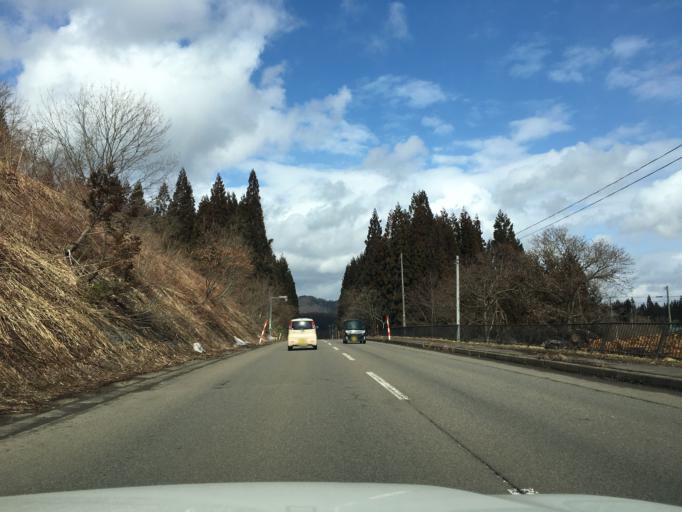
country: JP
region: Akita
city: Takanosu
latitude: 40.0206
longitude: 140.2750
